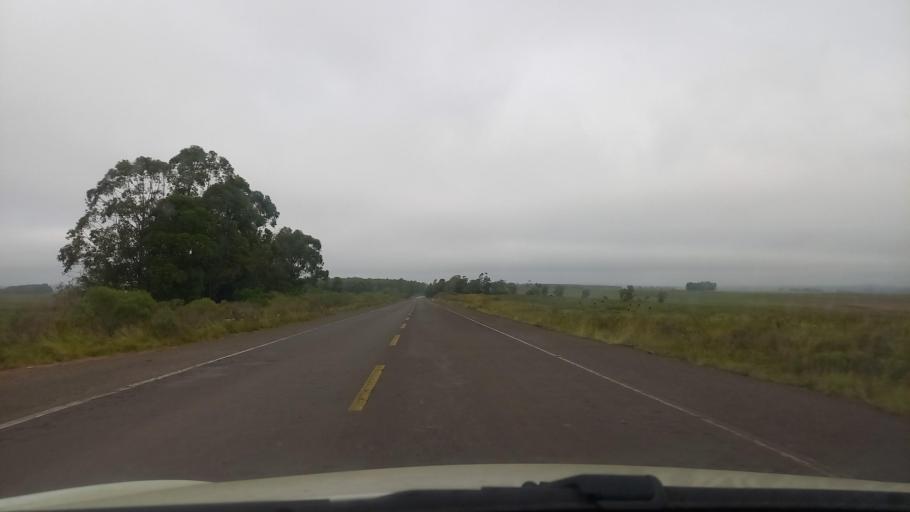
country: BR
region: Rio Grande do Sul
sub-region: Cacequi
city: Cacequi
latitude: -30.0564
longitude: -54.6036
